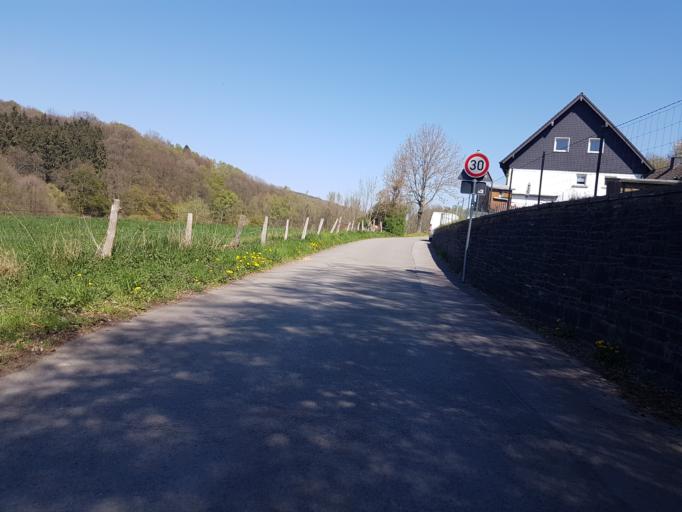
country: DE
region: North Rhine-Westphalia
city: Gevelsberg
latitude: 51.3809
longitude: 7.3103
